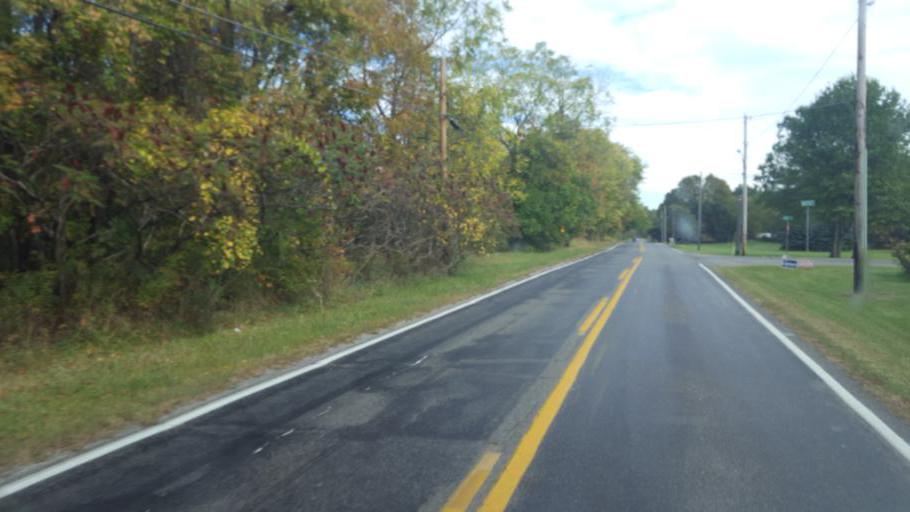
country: US
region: Ohio
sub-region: Lorain County
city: Vermilion-on-the-Lake
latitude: 41.3773
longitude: -82.3232
